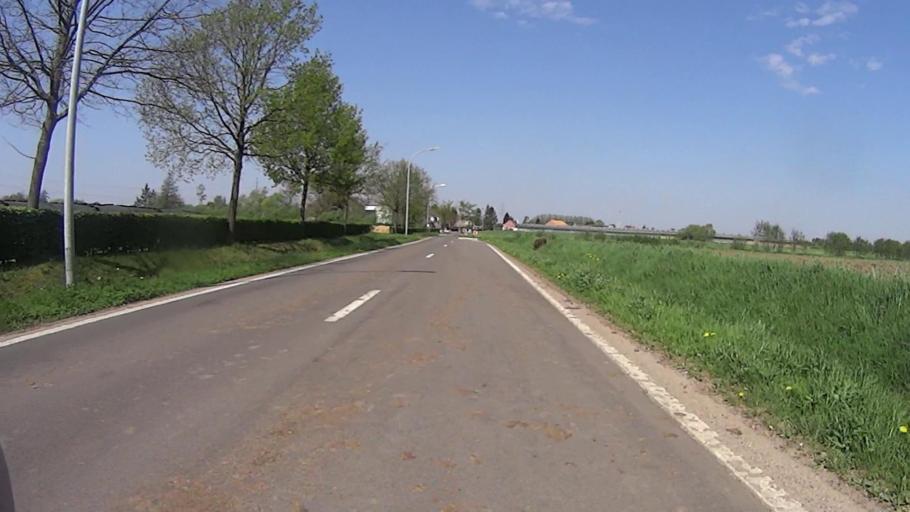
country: BE
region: Flanders
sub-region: Provincie Antwerpen
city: Sint-Amands
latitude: 51.0480
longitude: 4.2328
